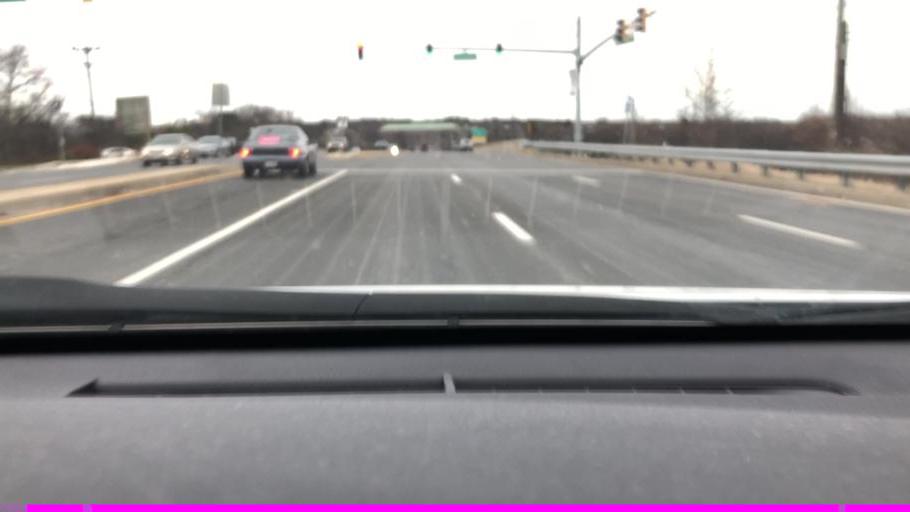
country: US
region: Maryland
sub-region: Prince George's County
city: Greenbelt
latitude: 38.9952
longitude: -76.8825
